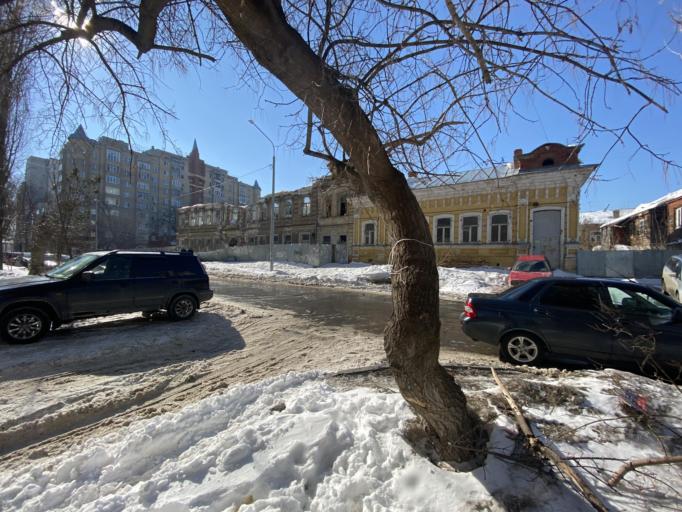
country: RU
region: Saratov
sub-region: Saratovskiy Rayon
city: Saratov
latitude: 51.5302
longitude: 46.0436
